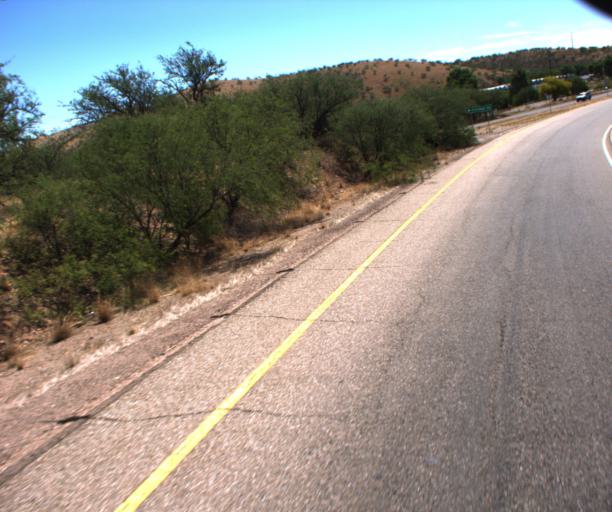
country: US
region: Arizona
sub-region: Santa Cruz County
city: Nogales
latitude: 31.3946
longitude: -110.9576
